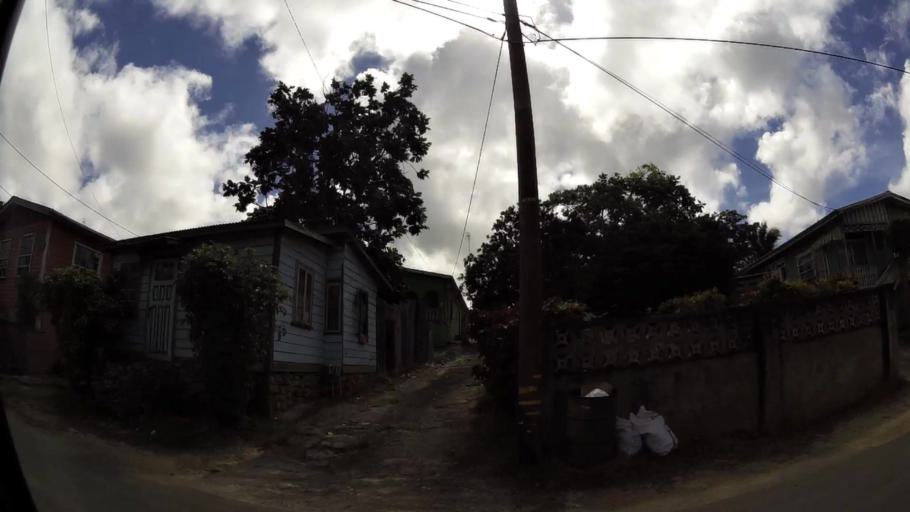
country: BB
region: Saint James
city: Holetown
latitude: 13.2050
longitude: -59.6063
